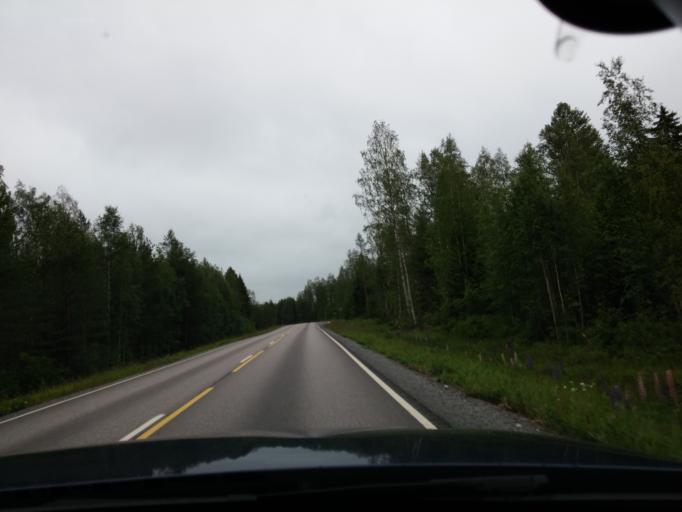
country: FI
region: Central Finland
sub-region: Saarijaervi-Viitasaari
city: Pylkoenmaeki
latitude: 62.6192
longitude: 24.7643
